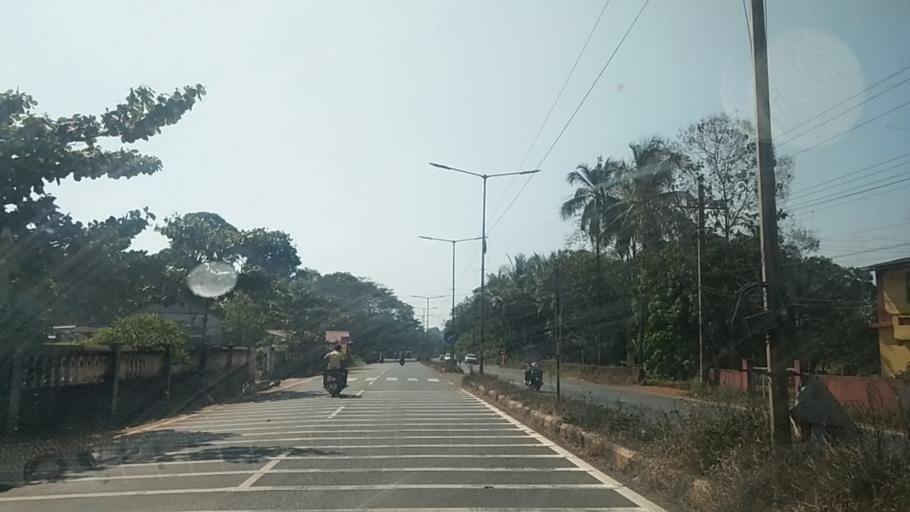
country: IN
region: Goa
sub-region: South Goa
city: Raia
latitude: 15.3030
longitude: 73.9749
